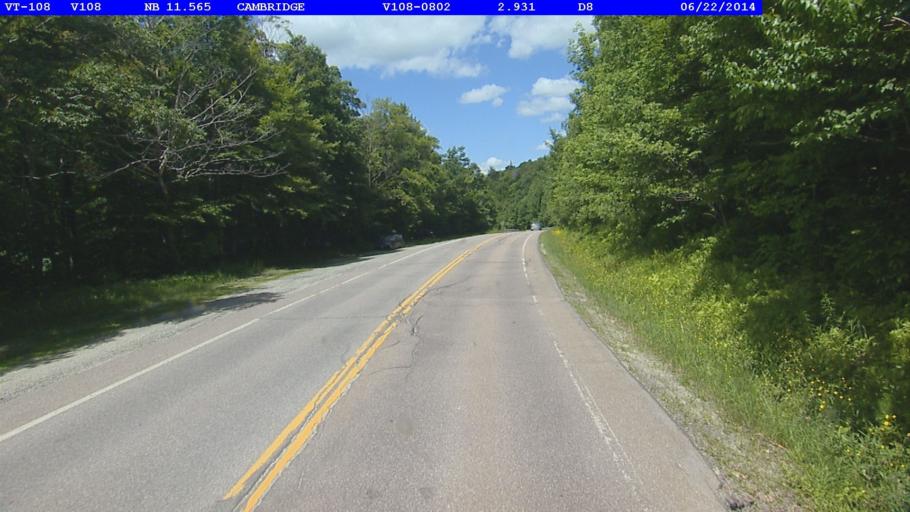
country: US
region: Vermont
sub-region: Lamoille County
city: Johnson
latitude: 44.5757
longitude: -72.7777
